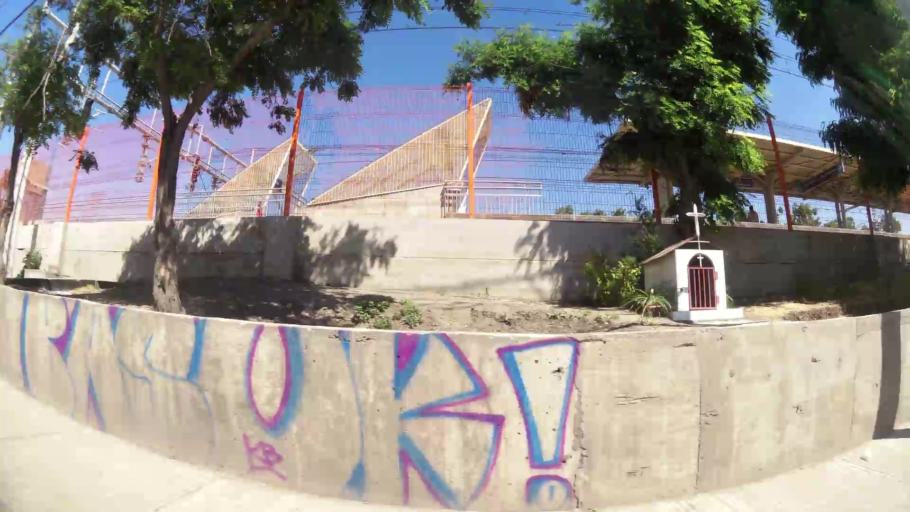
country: CL
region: Santiago Metropolitan
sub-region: Provincia de Maipo
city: San Bernardo
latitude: -33.6237
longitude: -70.7007
